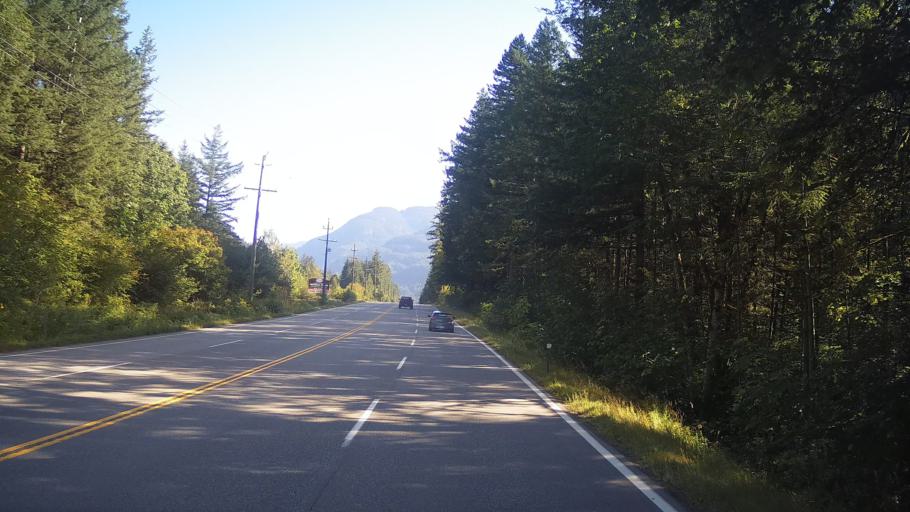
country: CA
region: British Columbia
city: Hope
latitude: 49.4664
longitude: -121.4312
